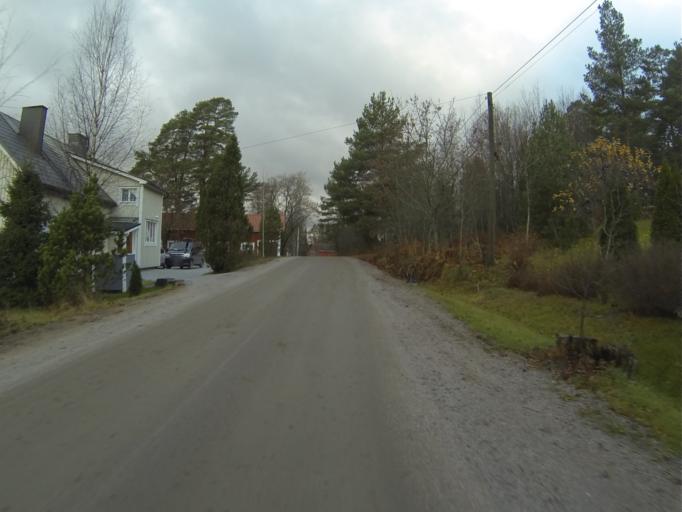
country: FI
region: Varsinais-Suomi
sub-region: Salo
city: Halikko
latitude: 60.4017
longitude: 23.0395
